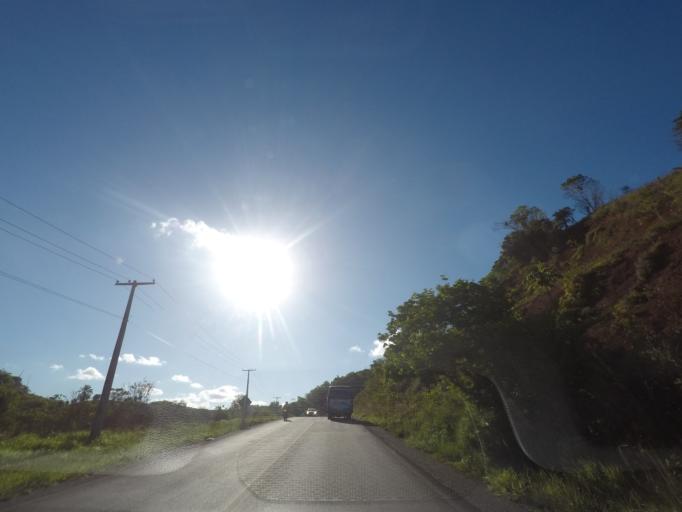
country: BR
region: Bahia
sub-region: Nazare
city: Nazare
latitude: -13.0414
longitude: -39.0114
